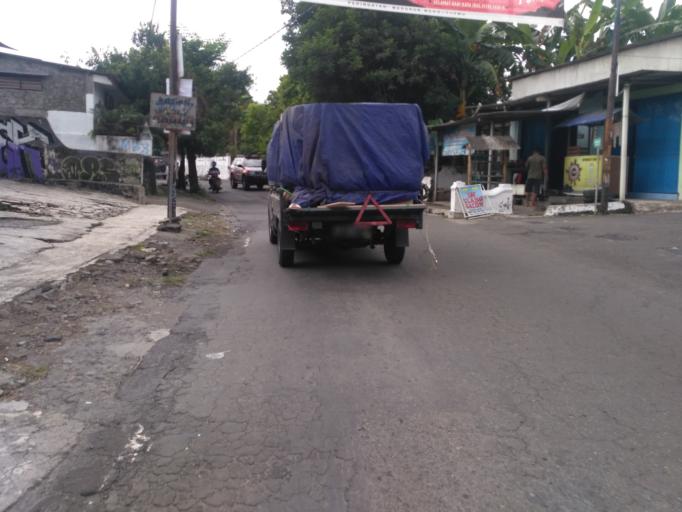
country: ID
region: Daerah Istimewa Yogyakarta
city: Sleman
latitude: -7.7234
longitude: 110.3581
